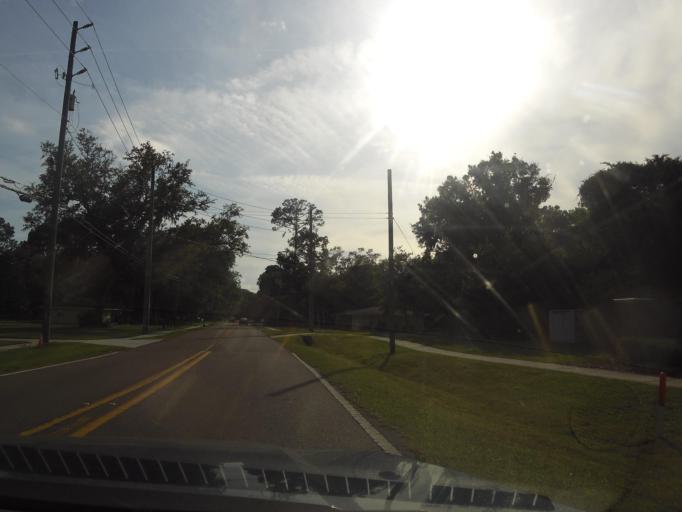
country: US
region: Florida
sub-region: Duval County
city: Jacksonville
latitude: 30.4640
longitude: -81.5576
